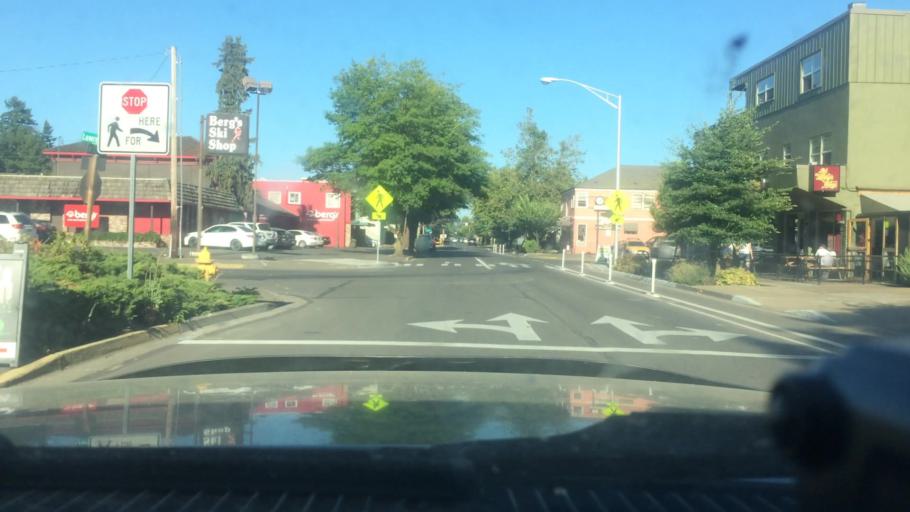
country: US
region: Oregon
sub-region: Lane County
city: Eugene
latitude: 44.0455
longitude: -123.0992
